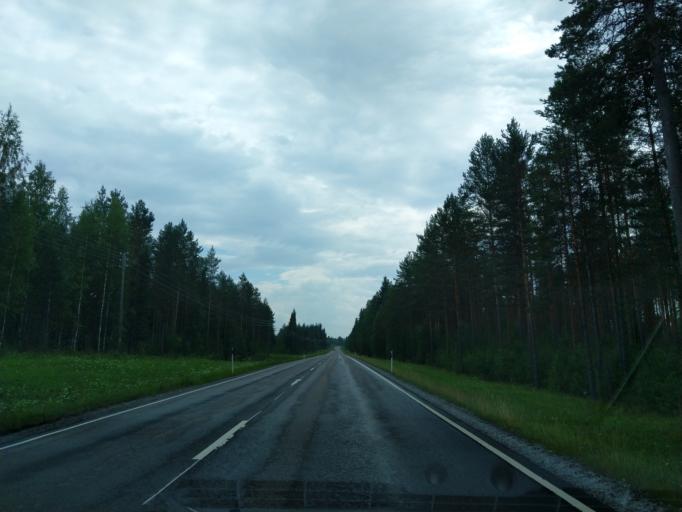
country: FI
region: Southern Savonia
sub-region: Savonlinna
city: Punkaharju
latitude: 61.6484
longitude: 29.4232
